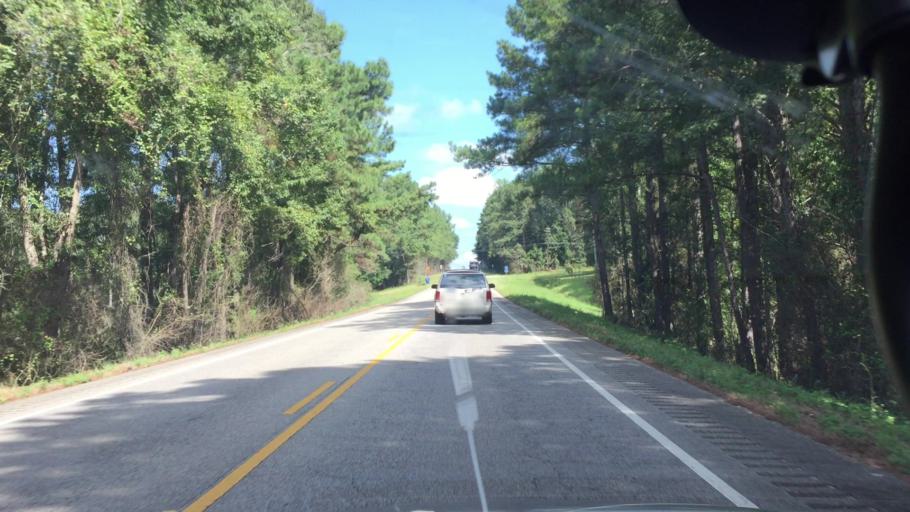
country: US
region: Alabama
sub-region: Coffee County
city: New Brockton
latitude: 31.4053
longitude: -85.8819
